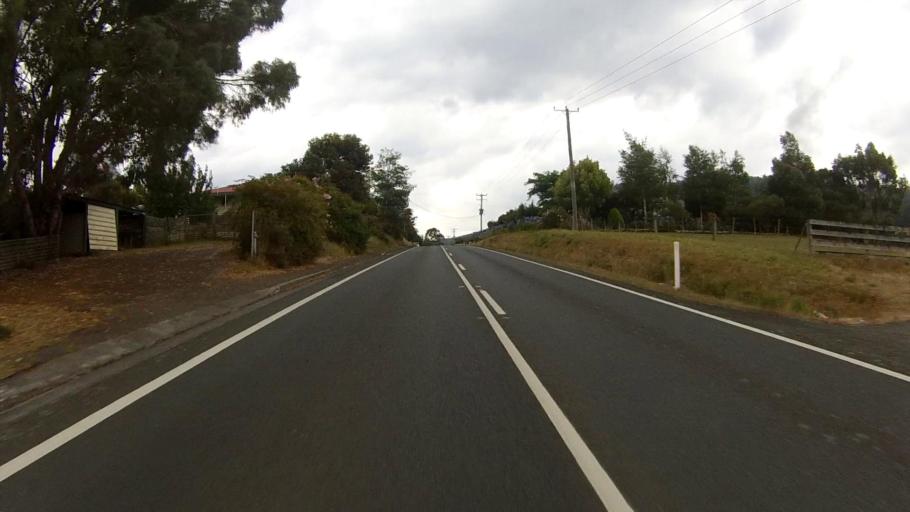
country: AU
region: Tasmania
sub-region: Huon Valley
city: Cygnet
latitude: -43.1467
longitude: 147.0662
